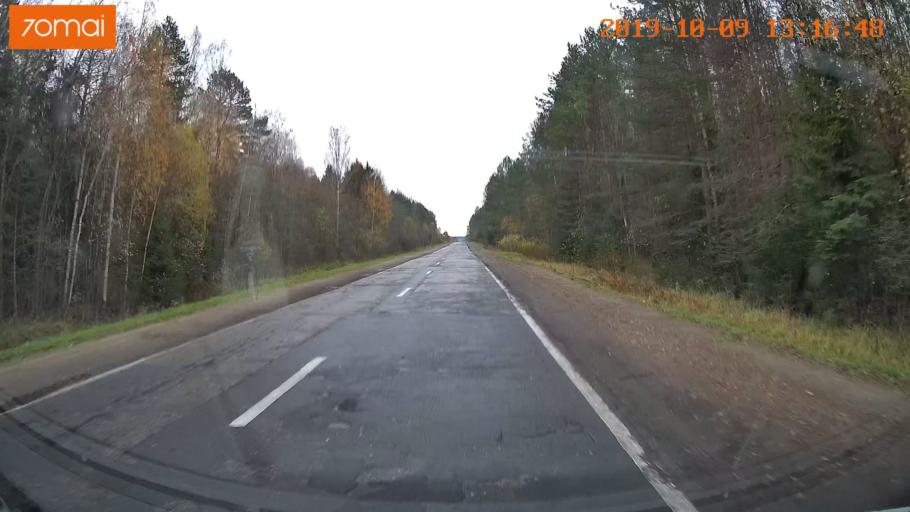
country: RU
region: Jaroslavl
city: Lyubim
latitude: 58.3585
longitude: 40.7708
